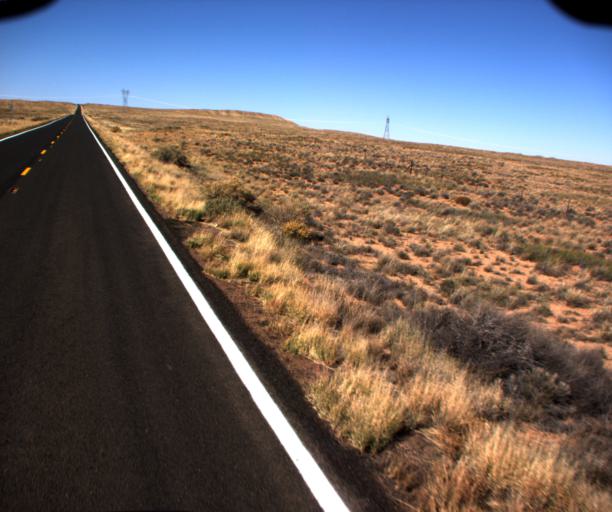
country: US
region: Arizona
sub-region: Coconino County
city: Tuba City
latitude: 35.9461
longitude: -110.9154
